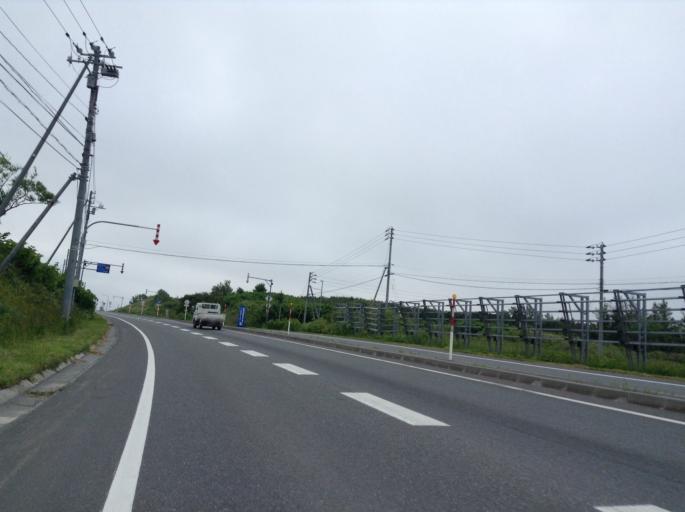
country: JP
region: Hokkaido
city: Wakkanai
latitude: 45.3755
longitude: 141.7130
